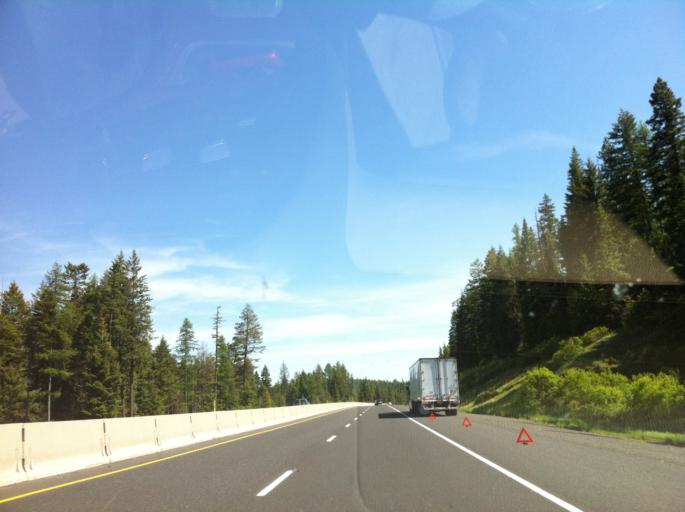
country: US
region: Oregon
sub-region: Umatilla County
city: Mission
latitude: 45.4766
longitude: -118.3987
